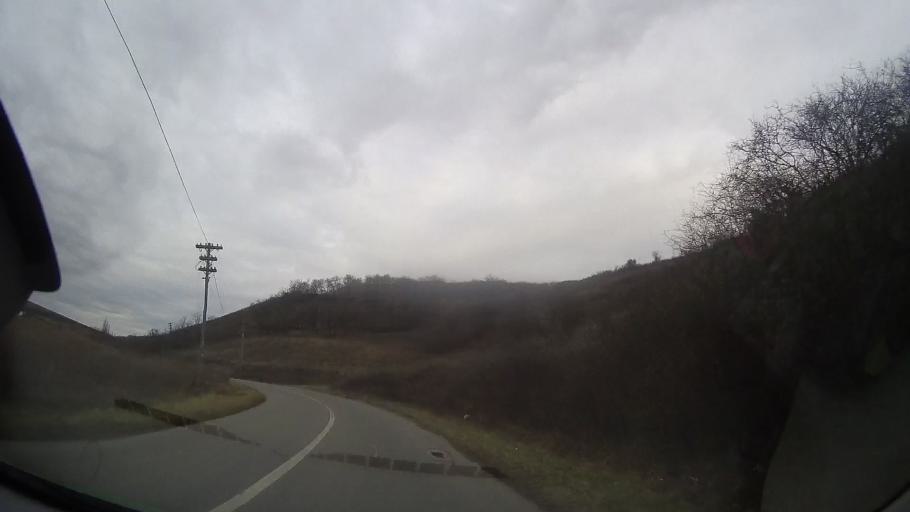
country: RO
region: Mures
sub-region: Comuna Faragau
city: Faragau
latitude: 46.7534
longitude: 24.5223
